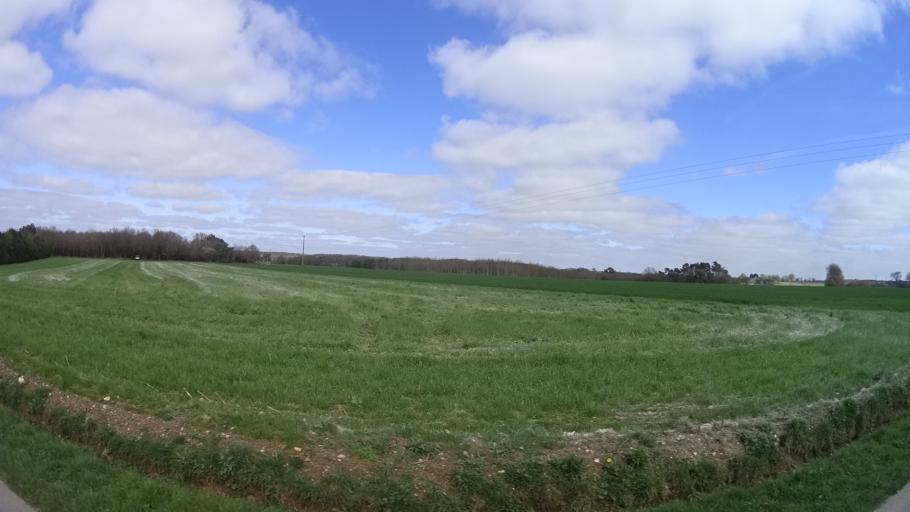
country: FR
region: Brittany
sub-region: Departement du Morbihan
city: Ruffiac
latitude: 47.8264
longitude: -2.2950
